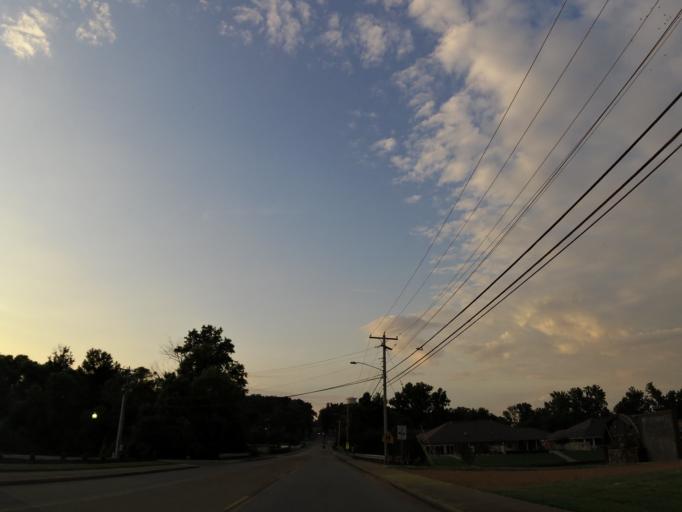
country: US
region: Tennessee
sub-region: Henry County
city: Paris
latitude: 36.2900
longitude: -88.3031
